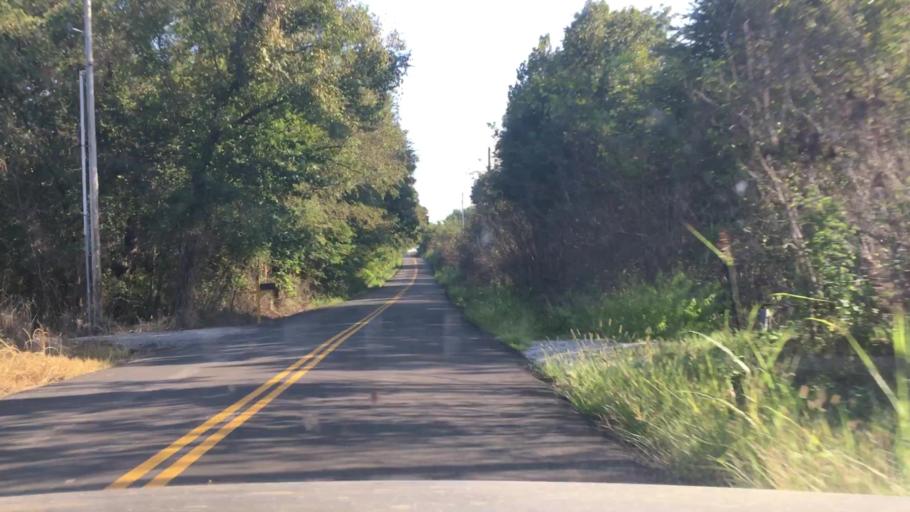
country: US
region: Oklahoma
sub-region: Muskogee County
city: Fort Gibson
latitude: 35.6425
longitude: -95.2160
